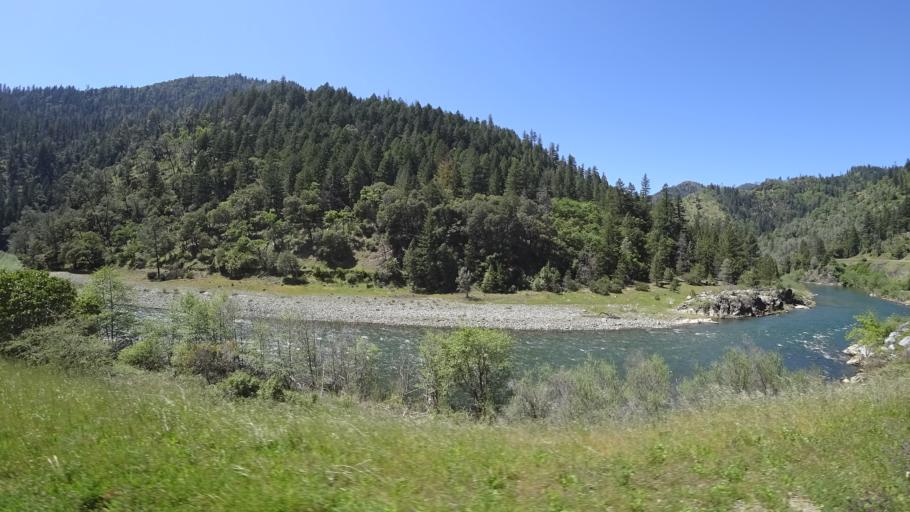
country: US
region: California
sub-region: Trinity County
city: Hayfork
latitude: 40.7879
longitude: -123.3477
